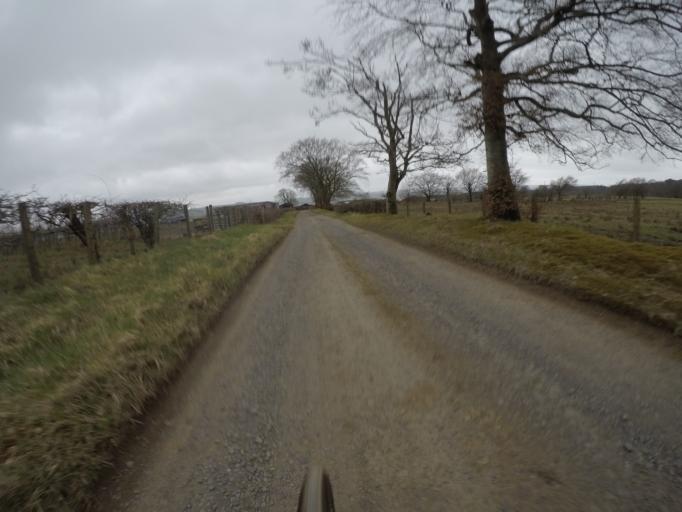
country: GB
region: Scotland
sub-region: East Ayrshire
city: Newmilns
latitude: 55.6250
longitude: -4.3438
